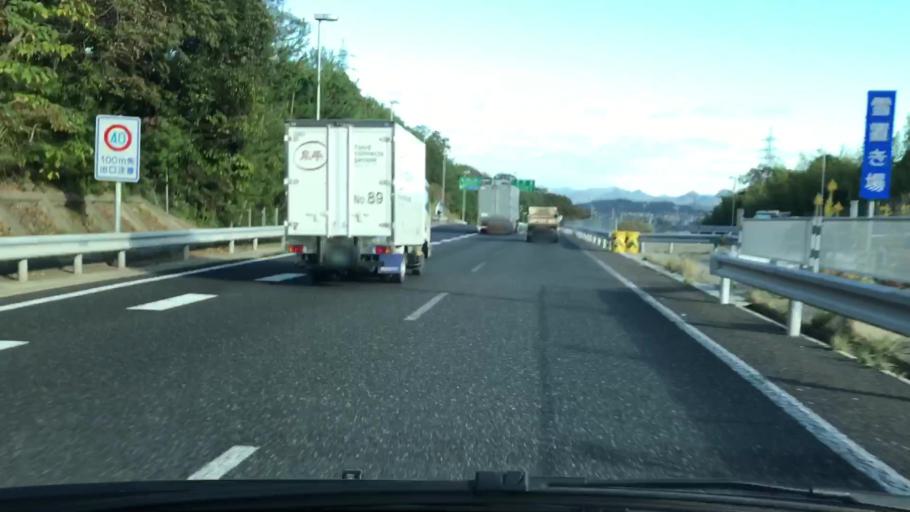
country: JP
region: Hyogo
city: Sandacho
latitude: 34.8129
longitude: 135.2471
